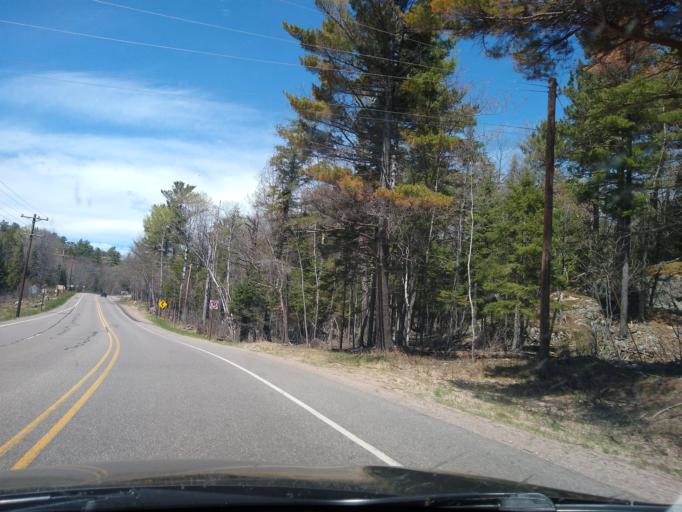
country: US
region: Michigan
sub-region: Marquette County
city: Trowbridge Park
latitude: 46.6015
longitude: -87.4582
